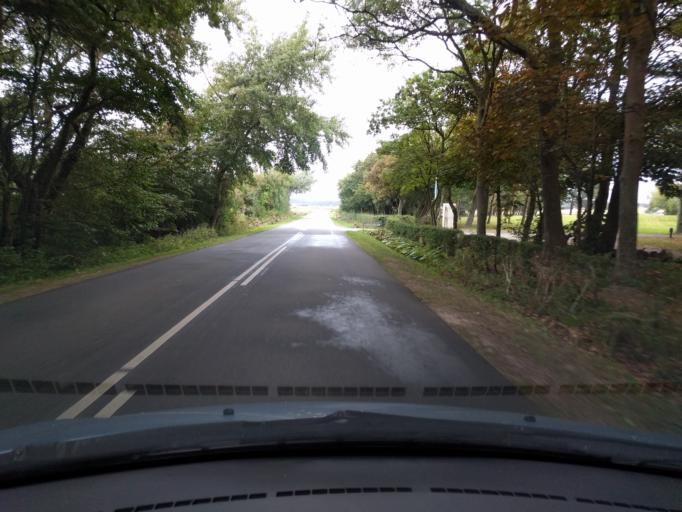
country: DK
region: South Denmark
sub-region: Assens Kommune
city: Assens
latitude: 55.1969
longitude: 9.9897
